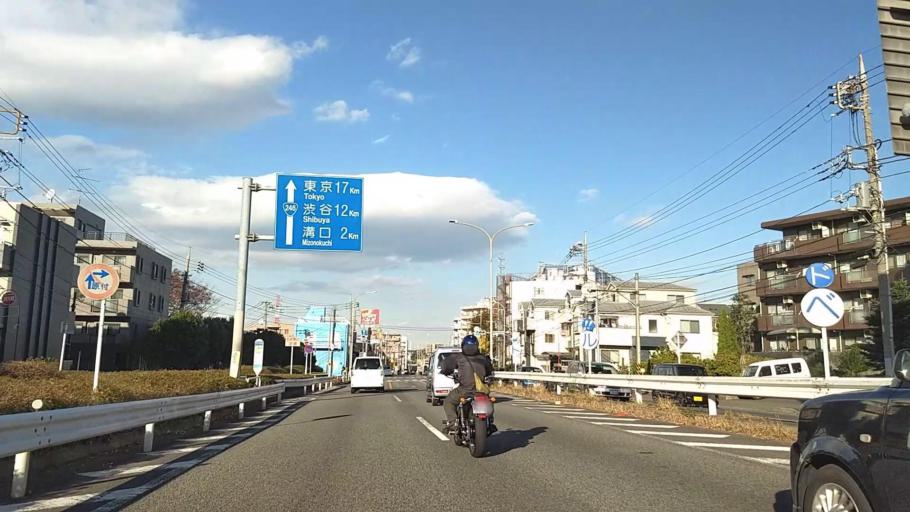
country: JP
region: Tokyo
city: Chofugaoka
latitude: 35.5946
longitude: 139.6023
